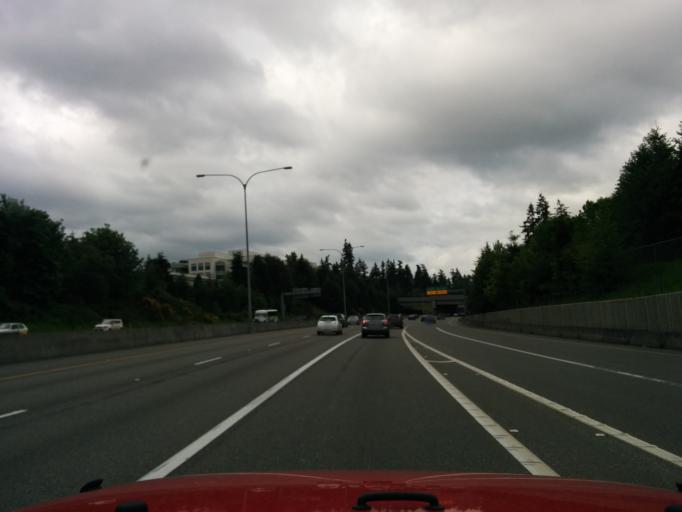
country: US
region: Washington
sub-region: King County
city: Redmond
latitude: 47.6421
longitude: -122.1345
